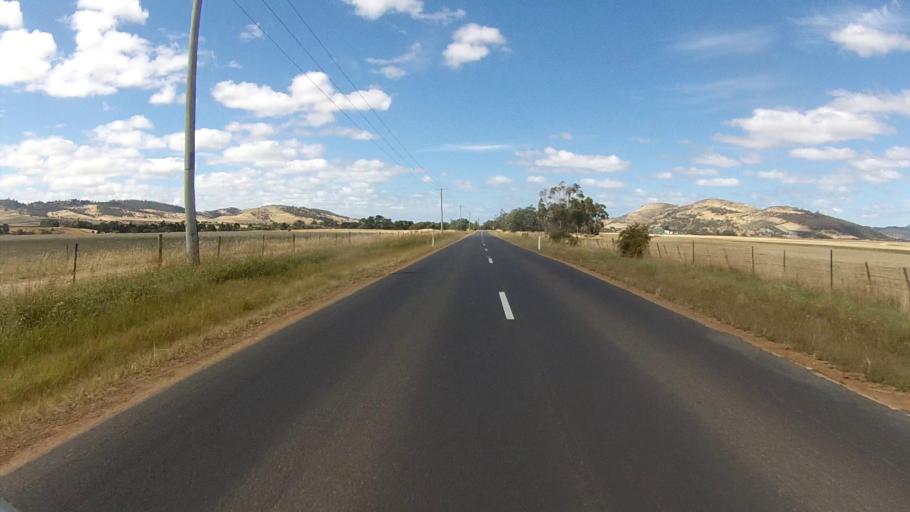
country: AU
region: Tasmania
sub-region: Clarence
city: Cambridge
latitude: -42.7209
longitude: 147.4341
